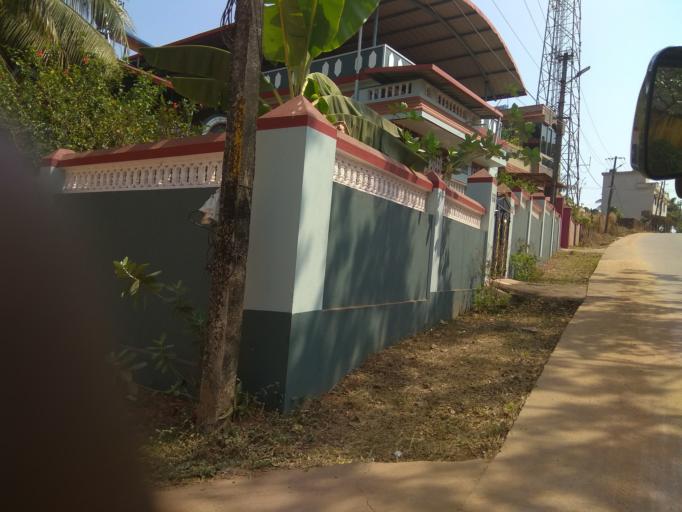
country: IN
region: Karnataka
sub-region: Dakshina Kannada
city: Mangalore
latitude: 12.9393
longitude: 74.8553
